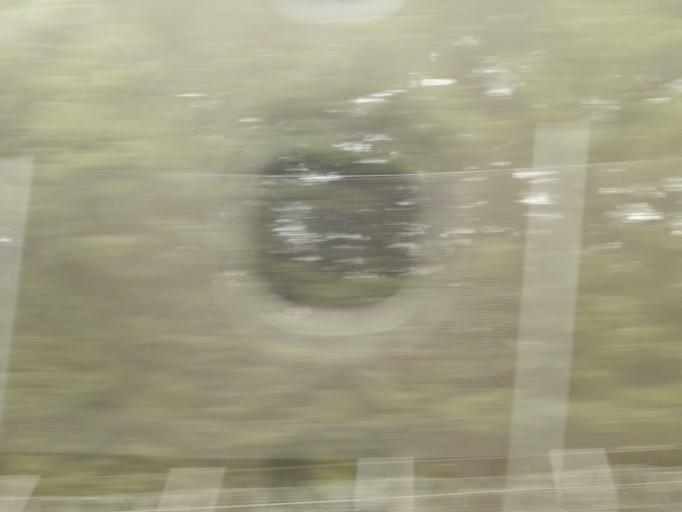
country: FR
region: Ile-de-France
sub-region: Departement du Val-de-Marne
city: Choisy-le-Roi
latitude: 48.7540
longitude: 2.4268
